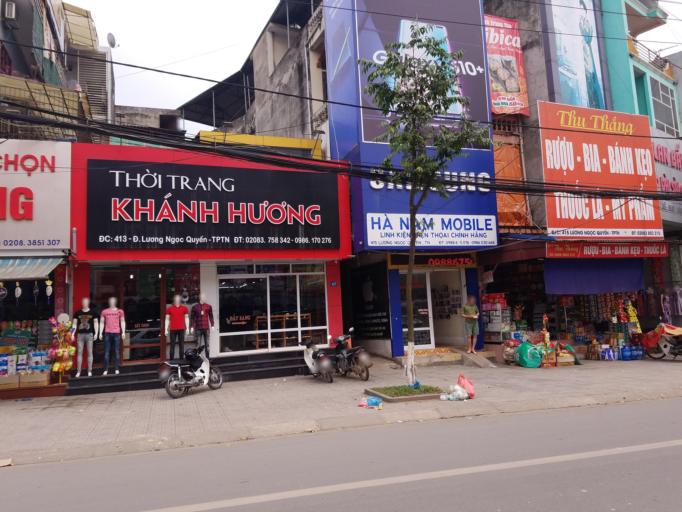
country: VN
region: Thai Nguyen
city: Thanh Pho Thai Nguyen
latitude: 21.5899
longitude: 105.8270
